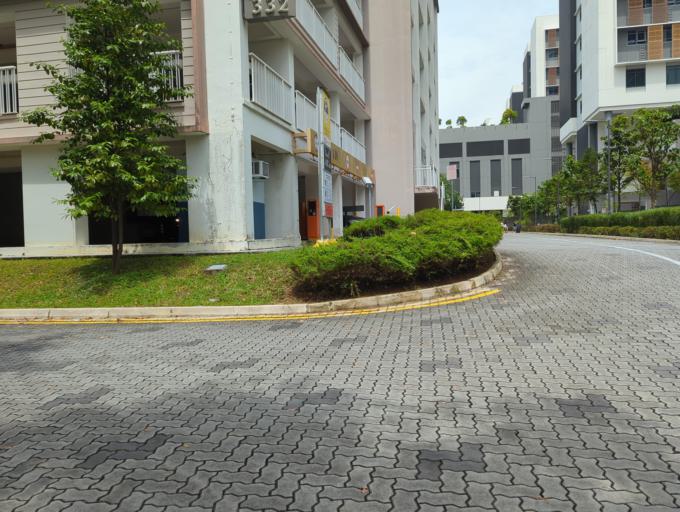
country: MY
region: Johor
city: Kampung Pasir Gudang Baru
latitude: 1.3944
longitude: 103.8924
